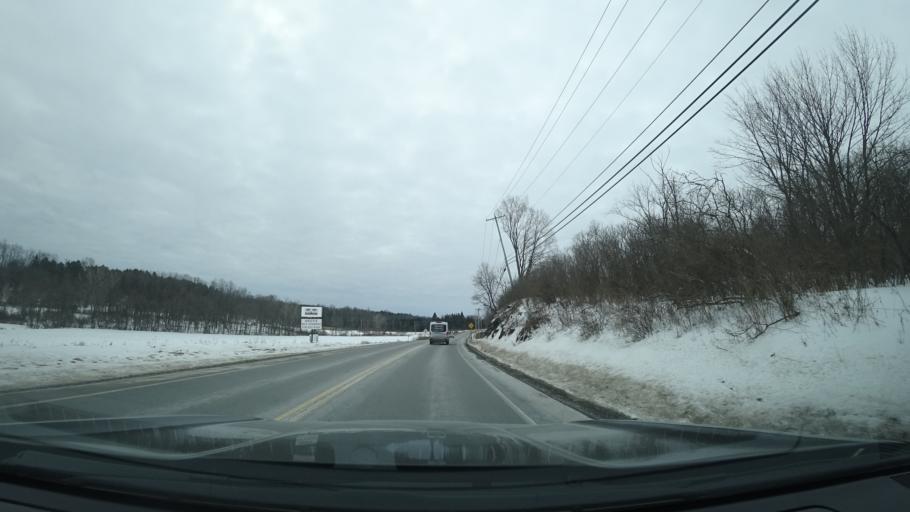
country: US
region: New York
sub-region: Washington County
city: Fort Edward
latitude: 43.2287
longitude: -73.4885
